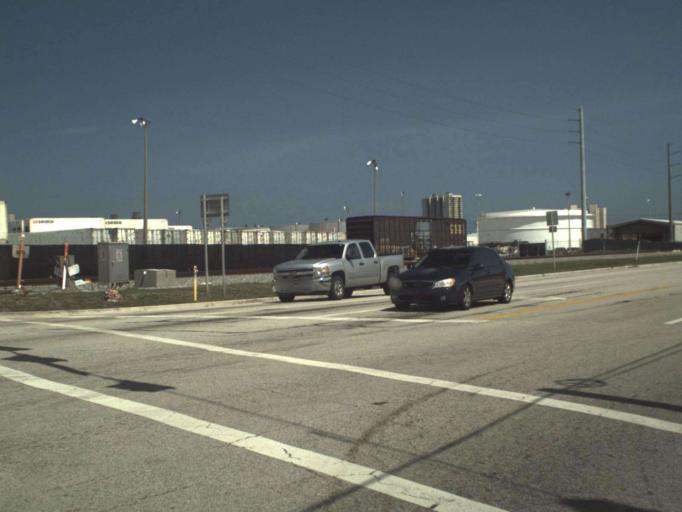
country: US
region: Florida
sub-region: Palm Beach County
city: Riviera Beach
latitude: 26.7691
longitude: -80.0615
